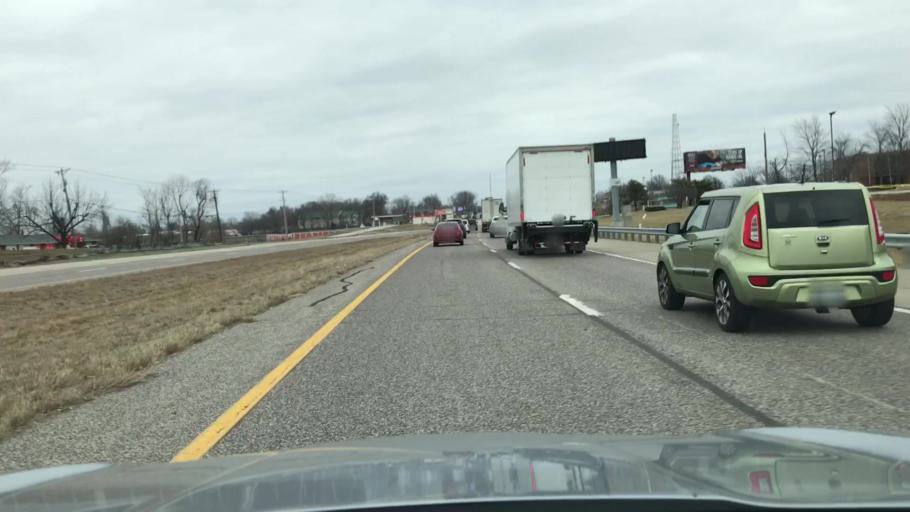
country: US
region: Missouri
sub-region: Saint Charles County
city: Saint Charles
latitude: 38.7707
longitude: -90.5218
